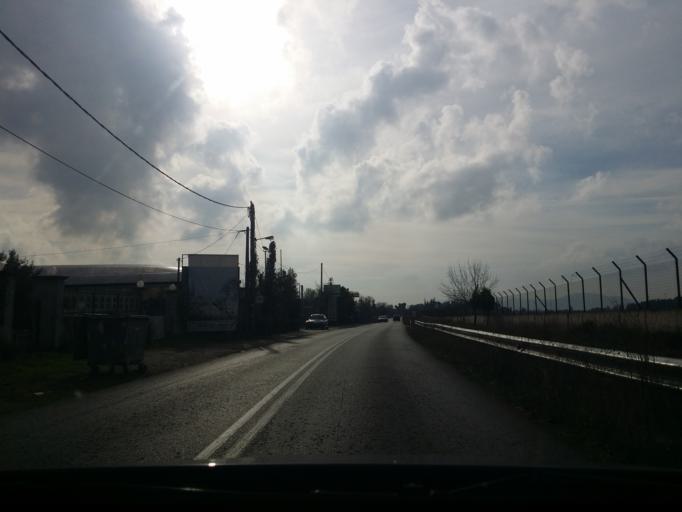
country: GR
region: Attica
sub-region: Nomarchia Anatolikis Attikis
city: Varybobi
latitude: 38.1055
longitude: 23.7879
